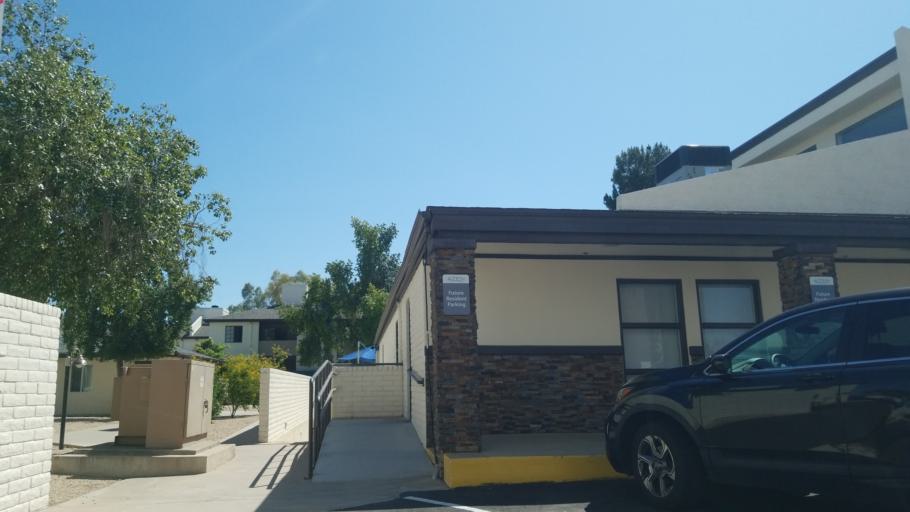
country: US
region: Arizona
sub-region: Maricopa County
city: Paradise Valley
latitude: 33.5935
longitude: -112.0268
